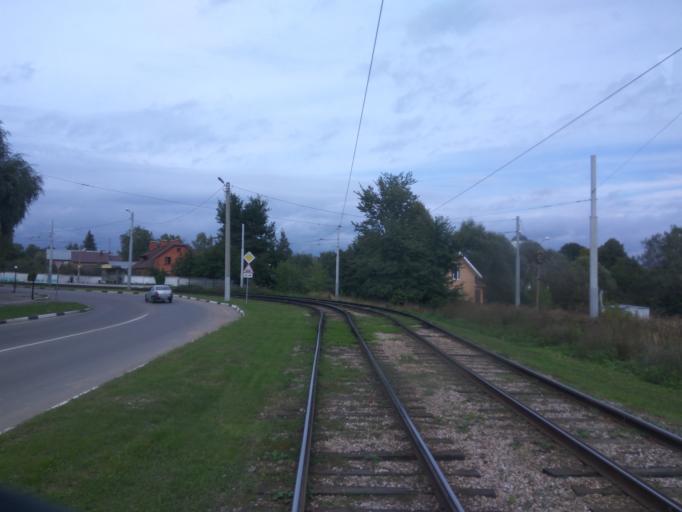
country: RU
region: Moskovskaya
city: Kolomna
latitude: 55.0602
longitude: 38.7573
